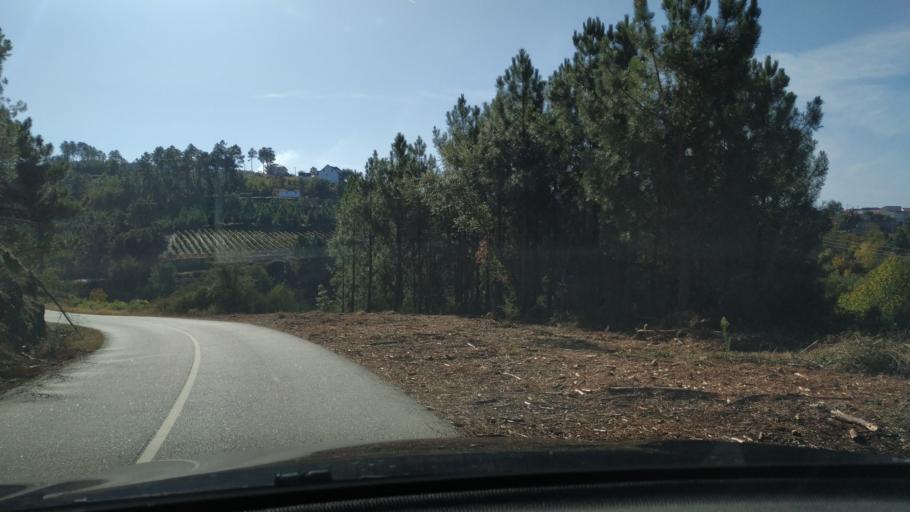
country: PT
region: Vila Real
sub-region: Sabrosa
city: Vilela
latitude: 41.2314
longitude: -7.6329
